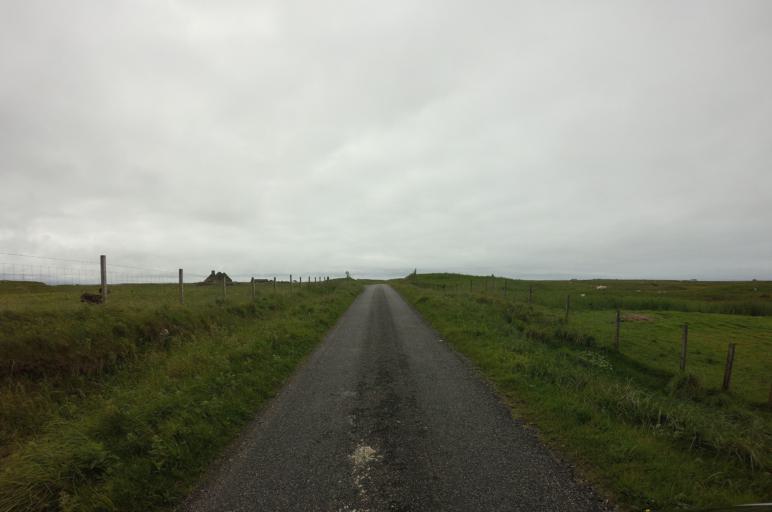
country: GB
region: Scotland
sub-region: Eilean Siar
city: Isle of North Uist
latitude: 57.5339
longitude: -7.3529
